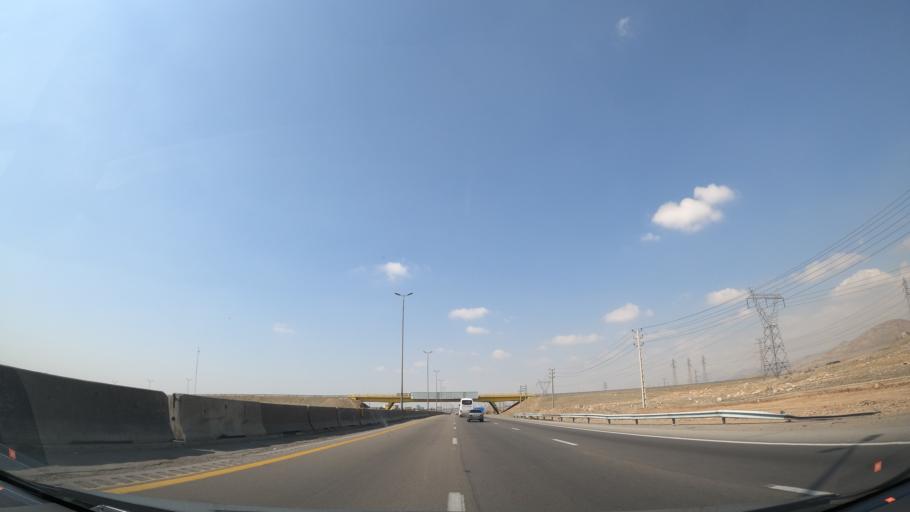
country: IR
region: Qazvin
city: Abyek
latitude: 36.0637
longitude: 50.4917
